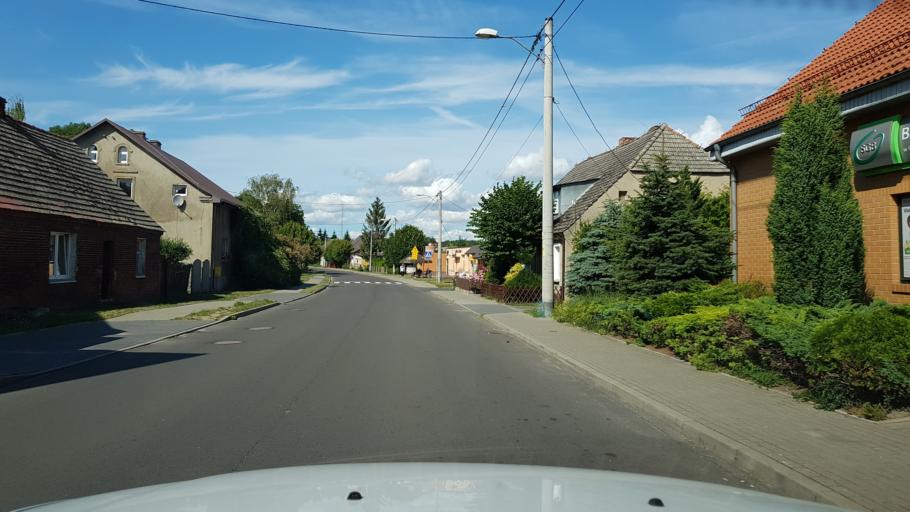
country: PL
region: West Pomeranian Voivodeship
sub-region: Powiat gryfinski
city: Stare Czarnowo
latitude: 53.2808
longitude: 14.7805
